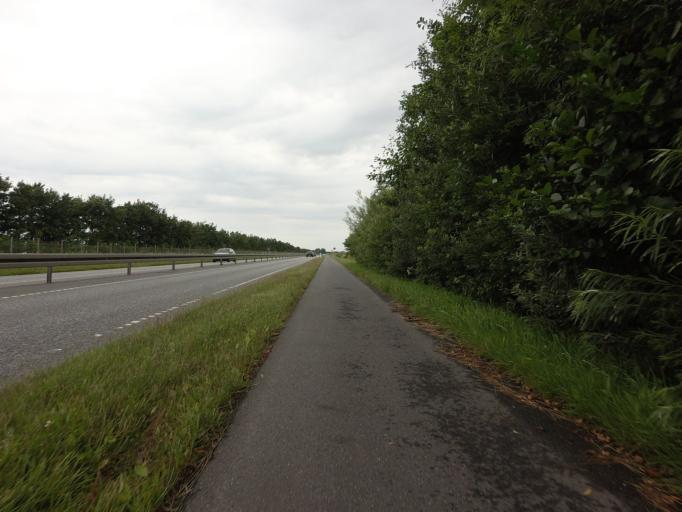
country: DK
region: North Denmark
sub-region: Alborg Kommune
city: Vadum
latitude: 57.0915
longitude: 9.8874
